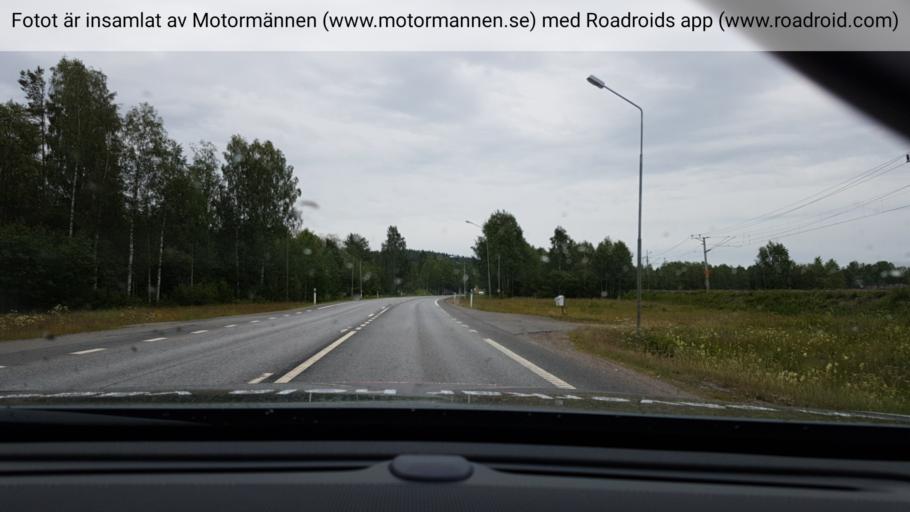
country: SE
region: Vaesterbotten
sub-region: Vannas Kommun
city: Vannasby
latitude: 63.9202
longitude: 19.8700
